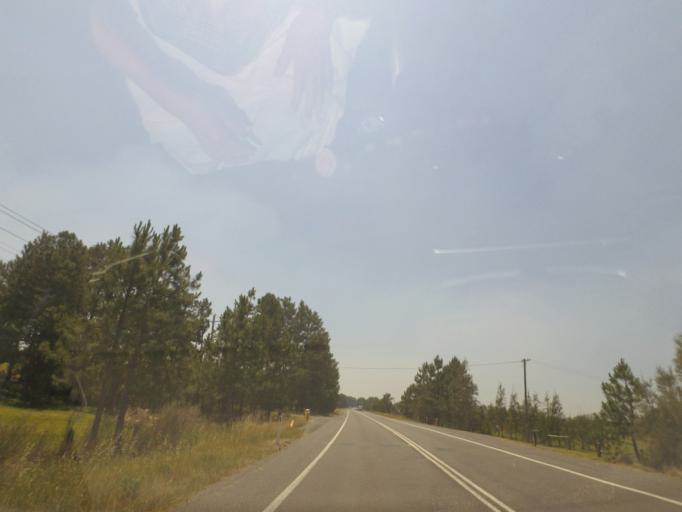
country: AU
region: New South Wales
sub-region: Port Stephens Shire
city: Medowie
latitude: -32.8065
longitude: 151.8756
